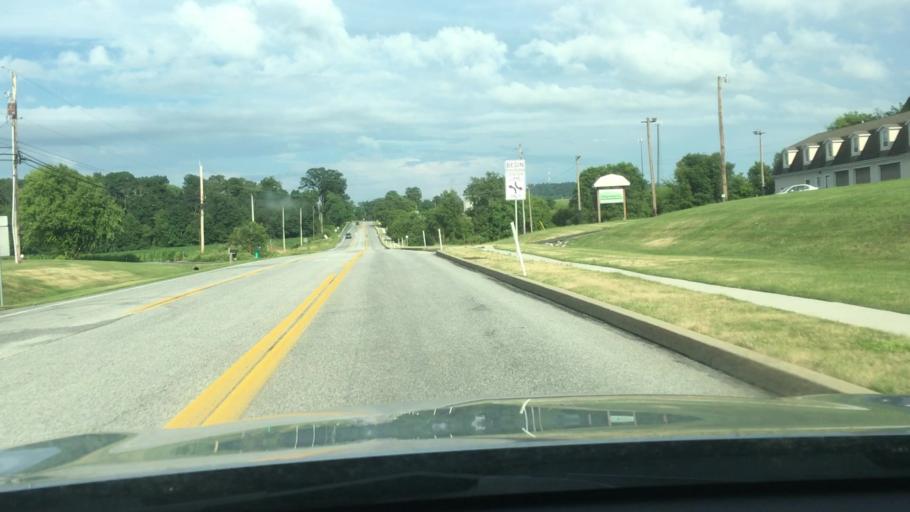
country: US
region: Pennsylvania
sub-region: York County
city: Dillsburg
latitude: 40.1057
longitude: -77.0233
